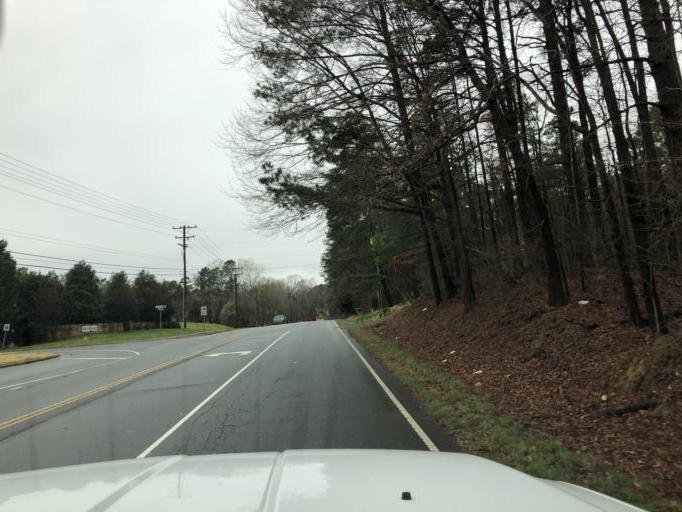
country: US
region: North Carolina
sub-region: Mecklenburg County
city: Huntersville
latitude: 35.3462
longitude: -80.8880
